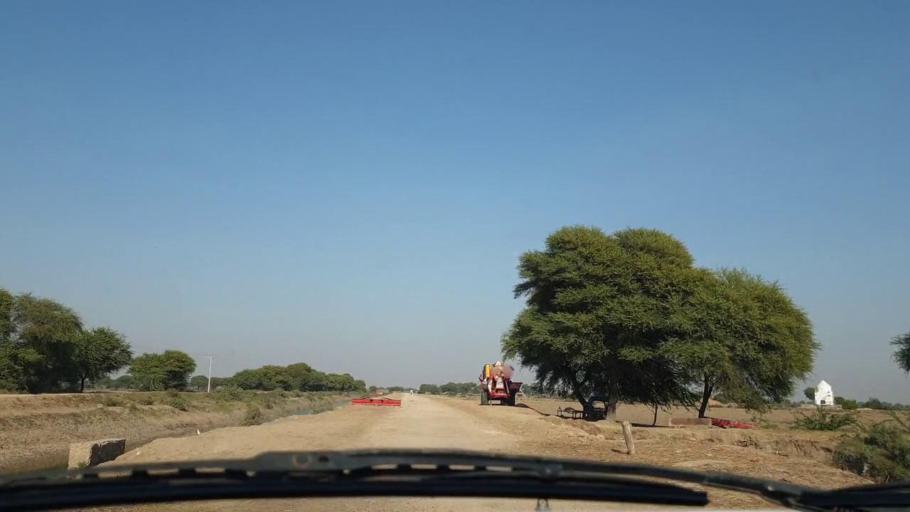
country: PK
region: Sindh
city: Bulri
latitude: 24.8030
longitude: 68.3920
